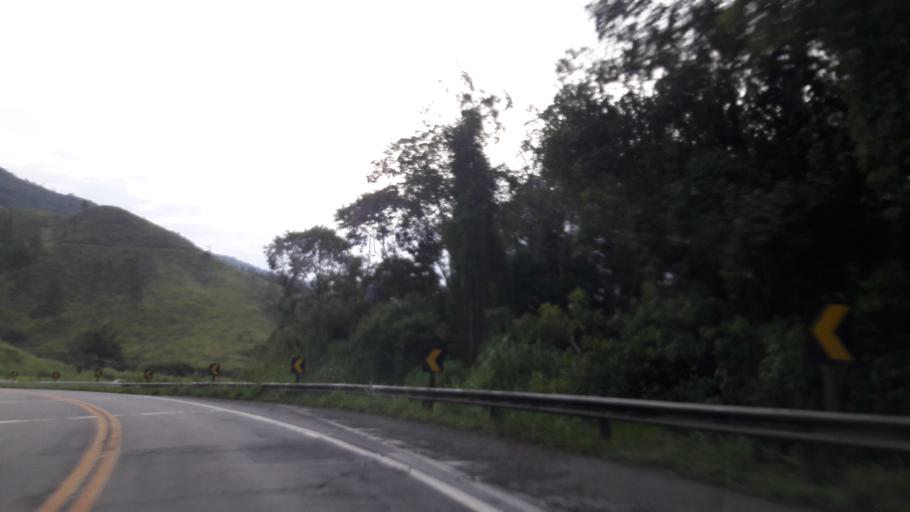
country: BR
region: Sao Paulo
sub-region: Miracatu
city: Miracatu
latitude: -24.2654
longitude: -47.2966
